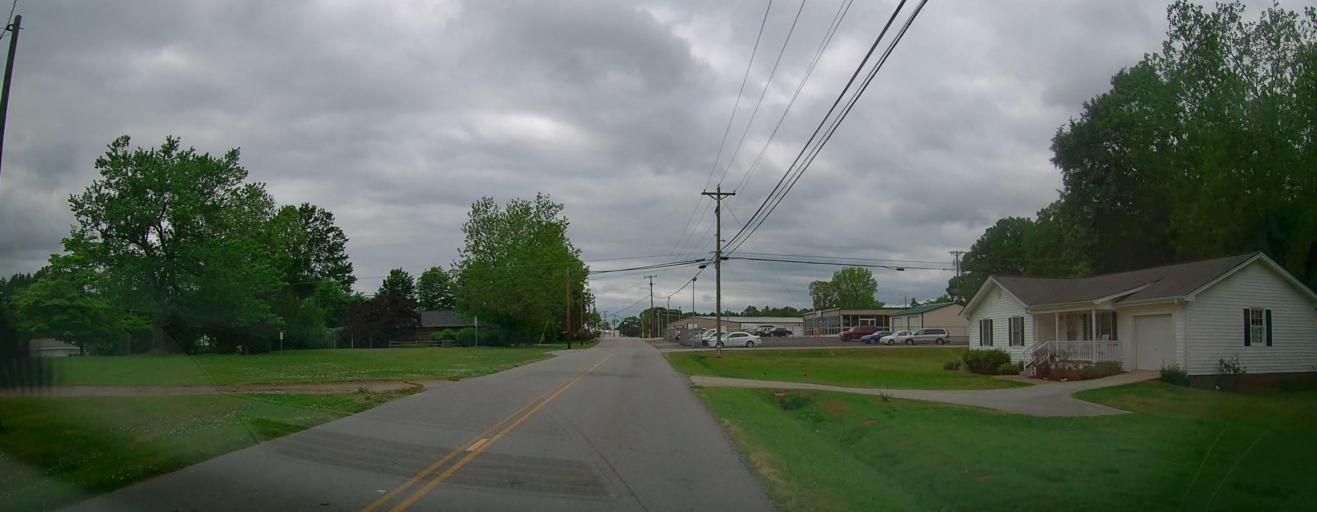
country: US
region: Georgia
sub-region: Walton County
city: Monroe
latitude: 33.7991
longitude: -83.6994
